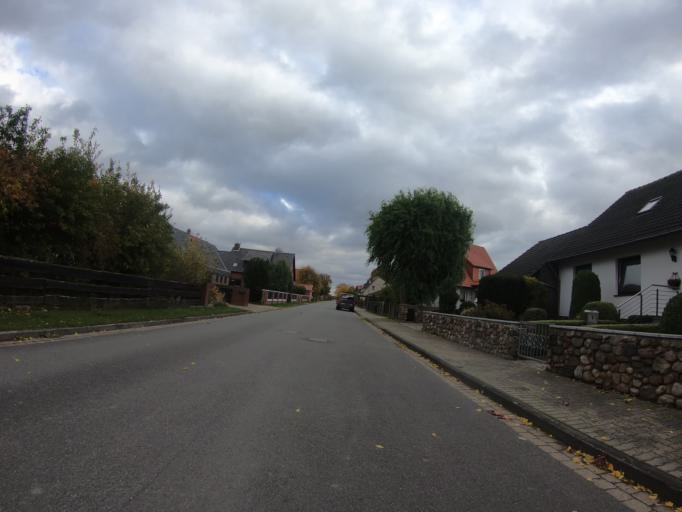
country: DE
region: Lower Saxony
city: Adenbuettel
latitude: 52.3776
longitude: 10.4858
